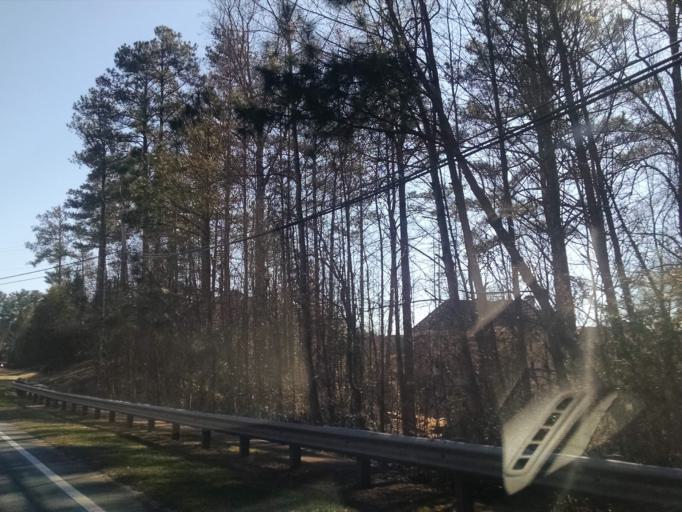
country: US
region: Georgia
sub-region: Gwinnett County
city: Suwanee
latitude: 34.0801
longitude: -84.0735
